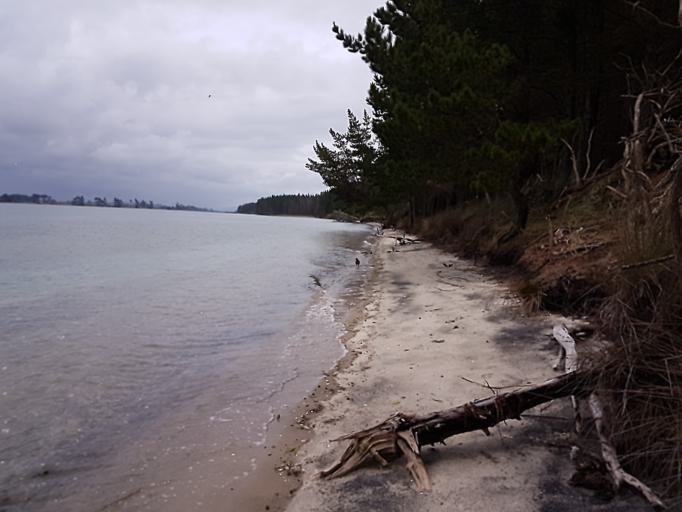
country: NZ
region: Bay of Plenty
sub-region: Tauranga City
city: Tauranga
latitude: -37.6374
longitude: 176.1416
